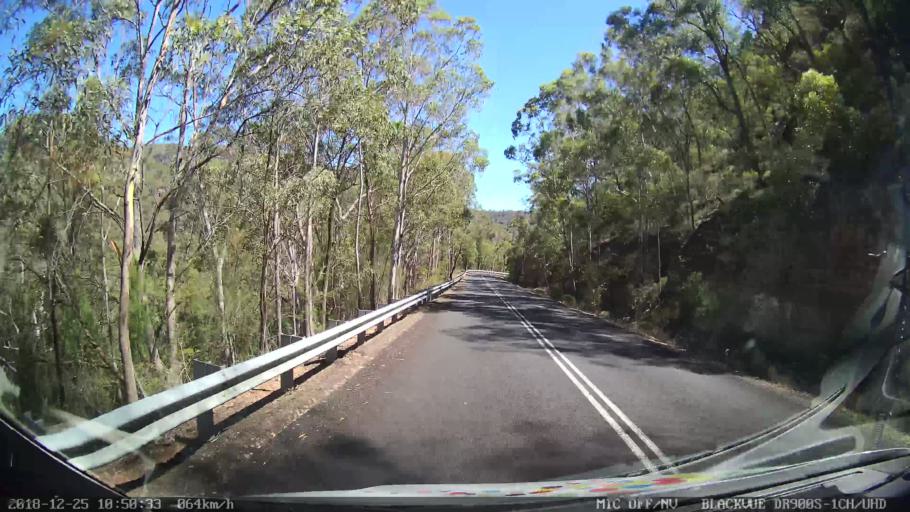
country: AU
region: New South Wales
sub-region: Upper Hunter Shire
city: Merriwa
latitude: -32.4451
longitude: 150.2679
